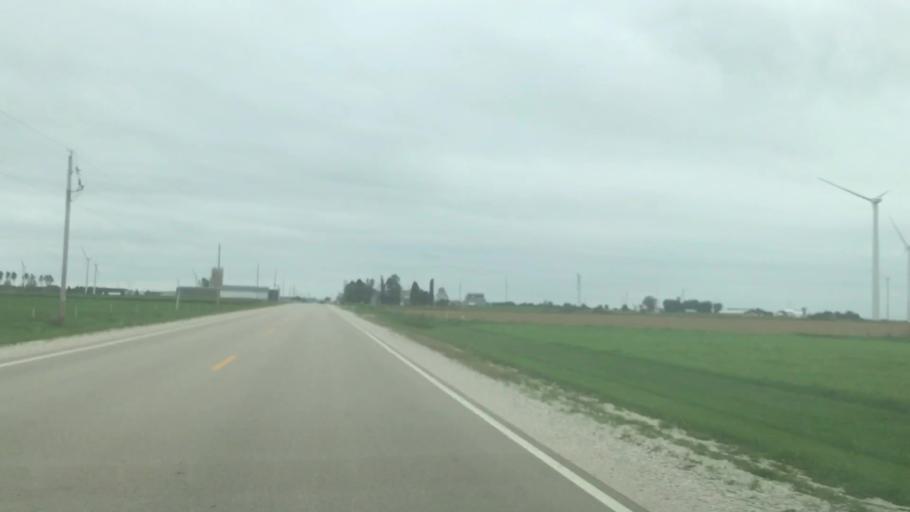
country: US
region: Wisconsin
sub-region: Fond du Lac County
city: Oakfield
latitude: 43.6258
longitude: -88.5417
